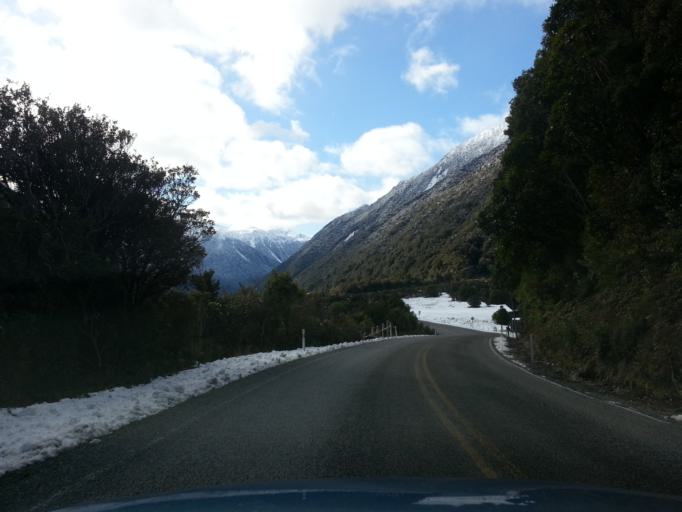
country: NZ
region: West Coast
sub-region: Grey District
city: Greymouth
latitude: -42.8554
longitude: 171.5594
